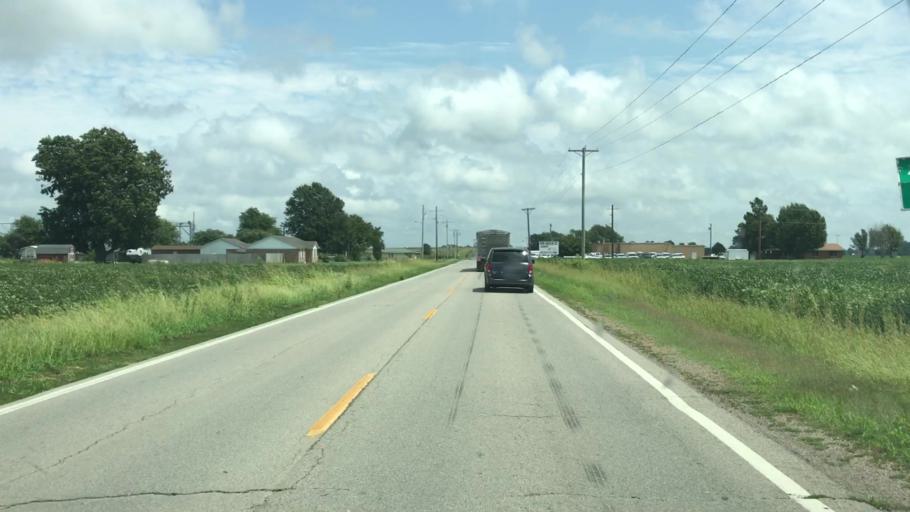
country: US
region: Missouri
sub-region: Pemiscot County
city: Caruthersville
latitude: 36.1762
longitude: -89.7020
